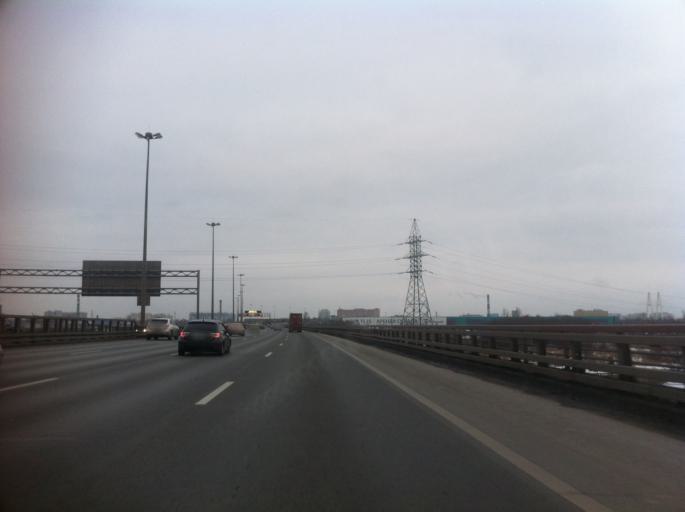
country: RU
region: St.-Petersburg
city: Obukhovo
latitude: 59.8390
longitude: 30.4534
